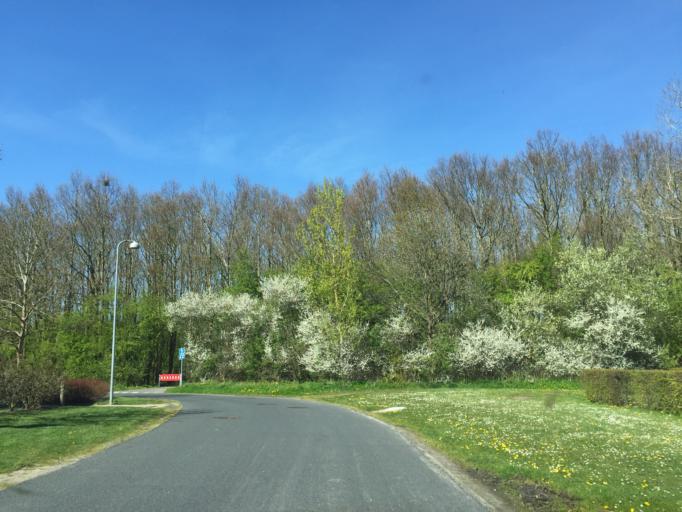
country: DK
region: South Denmark
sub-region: Odense Kommune
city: Odense
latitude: 55.3698
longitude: 10.4067
